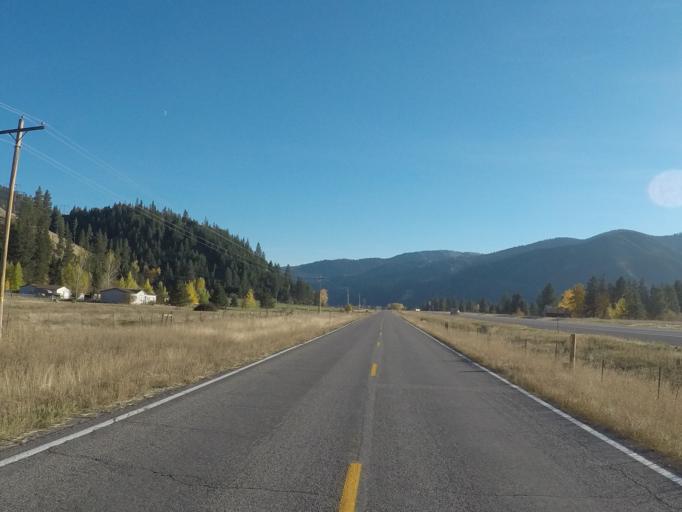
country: US
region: Montana
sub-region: Missoula County
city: Clinton
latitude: 46.7733
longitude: -113.7106
